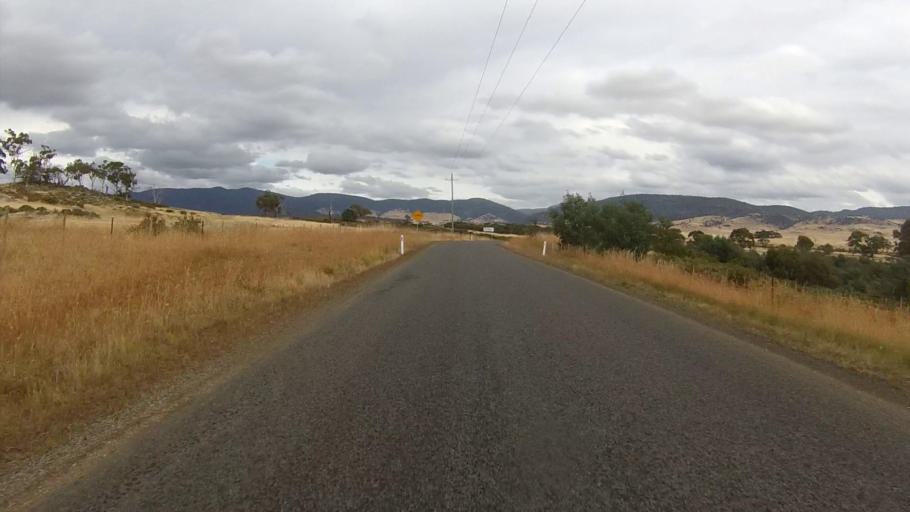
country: AU
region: Tasmania
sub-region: Northern Midlands
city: Evandale
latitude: -41.8094
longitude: 147.7537
